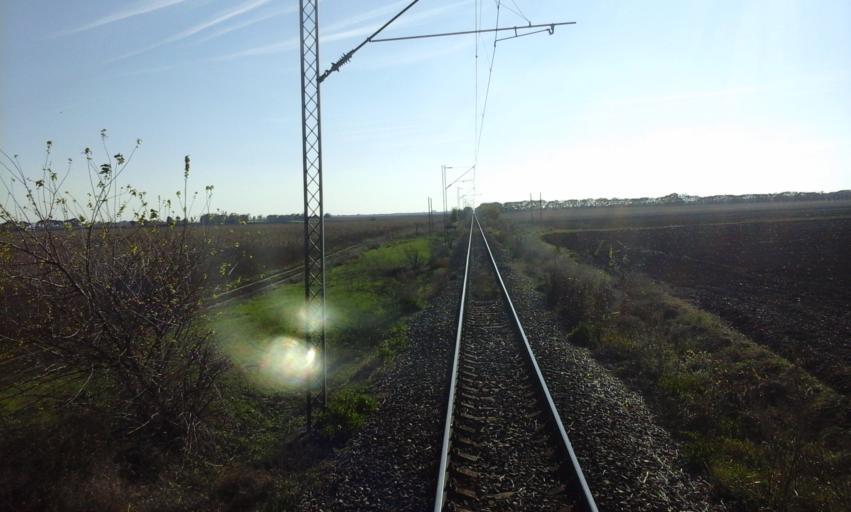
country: RS
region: Autonomna Pokrajina Vojvodina
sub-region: Severnobacki Okrug
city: Backa Topola
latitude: 45.8891
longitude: 19.6605
